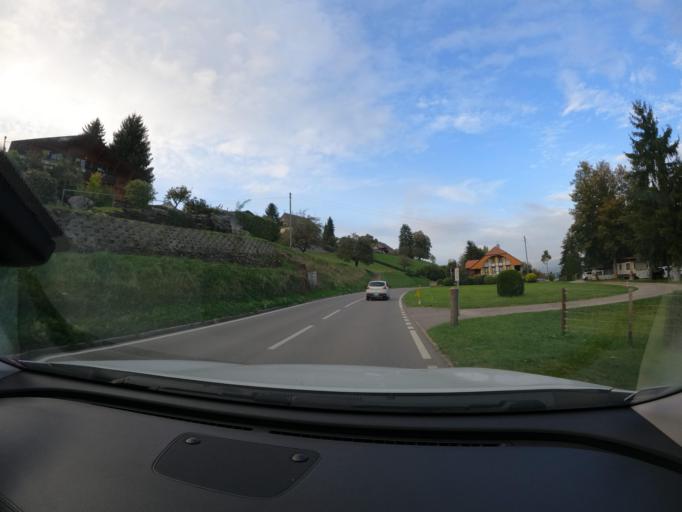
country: CH
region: Bern
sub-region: Bern-Mittelland District
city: Toffen
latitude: 46.8699
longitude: 7.4913
